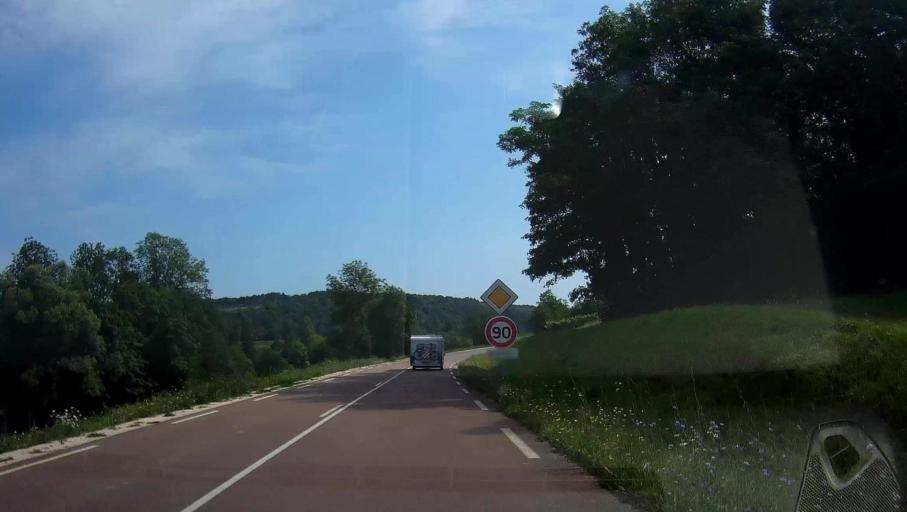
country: FR
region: Bourgogne
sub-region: Departement de la Cote-d'Or
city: Meursault
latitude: 46.9863
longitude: 4.7200
